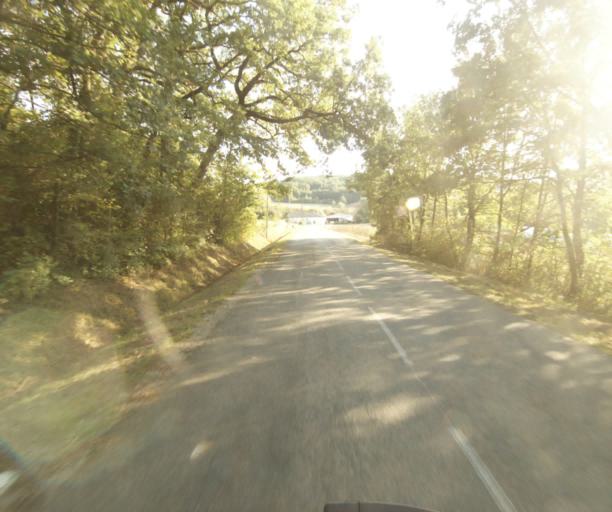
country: FR
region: Midi-Pyrenees
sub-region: Departement de la Haute-Garonne
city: Launac
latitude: 43.8210
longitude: 1.1342
